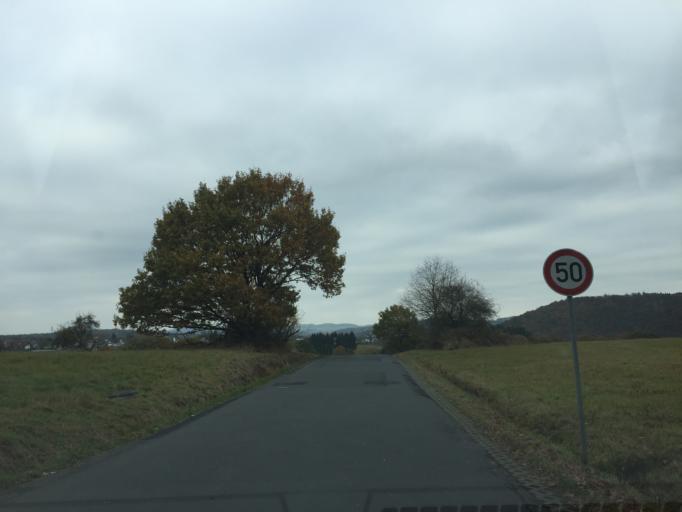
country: DE
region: Rheinland-Pfalz
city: Heiligenroth
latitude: 50.4396
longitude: 7.8635
